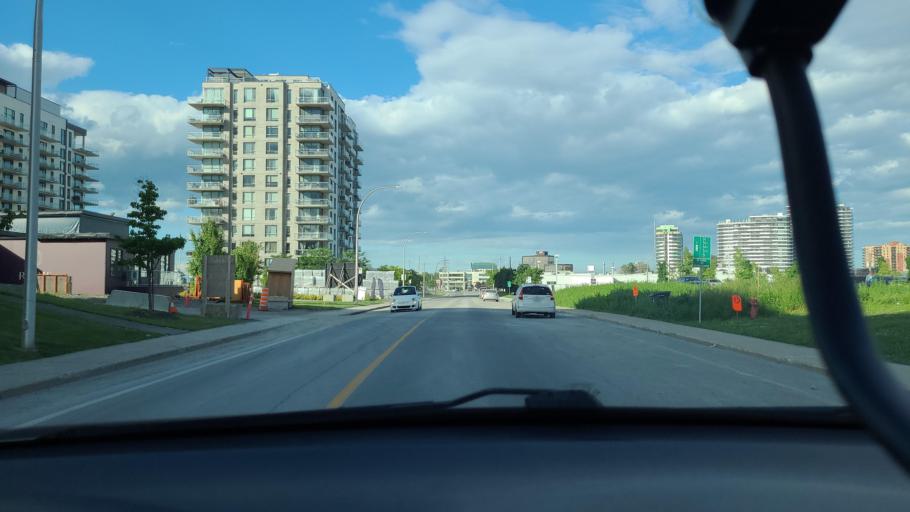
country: CA
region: Quebec
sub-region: Laval
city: Laval
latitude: 45.5630
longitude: -73.7652
